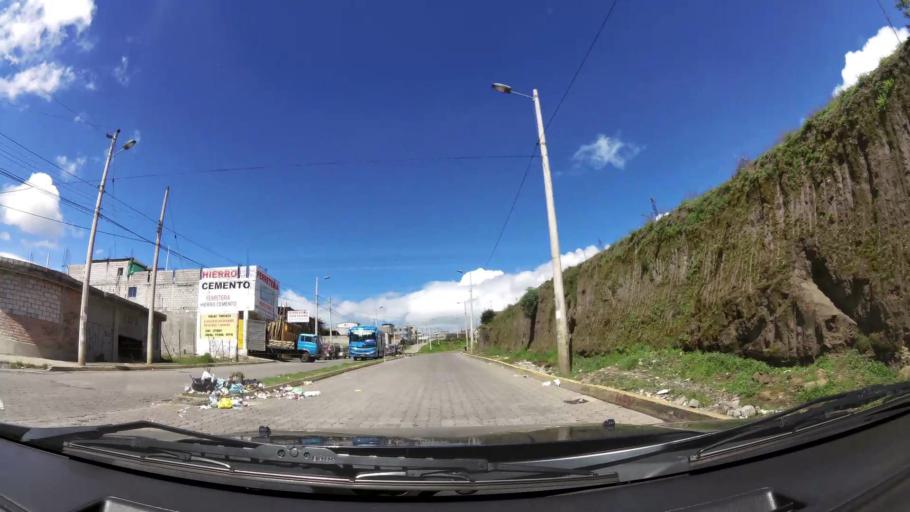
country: EC
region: Pichincha
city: Quito
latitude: -0.3263
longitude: -78.5666
